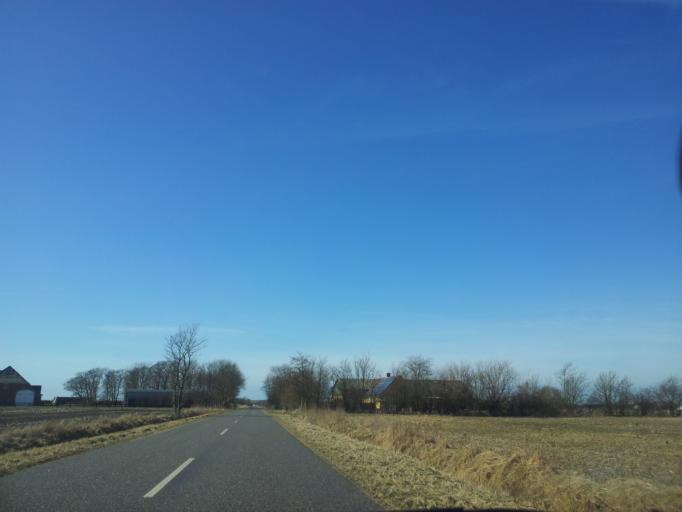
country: DK
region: South Denmark
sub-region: Tonder Kommune
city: Sherrebek
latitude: 55.1685
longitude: 8.7421
